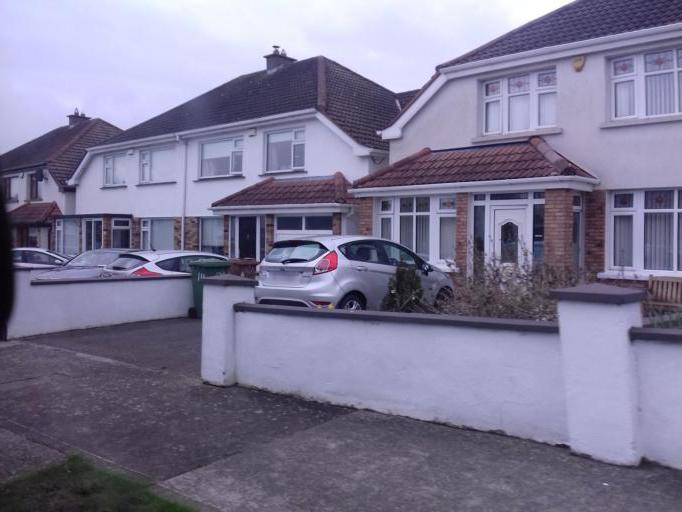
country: IE
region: Leinster
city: Portmarnock
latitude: 53.4275
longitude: -6.1366
